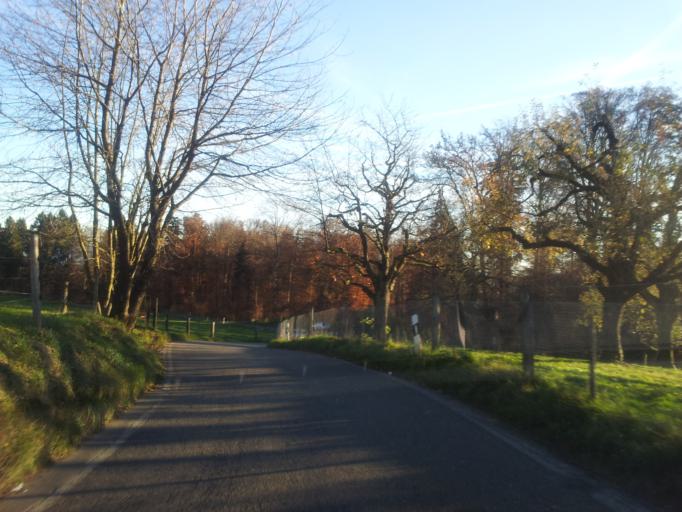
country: CH
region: Zurich
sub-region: Bezirk Dielsdorf
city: Daenikon
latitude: 47.4368
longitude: 8.3874
